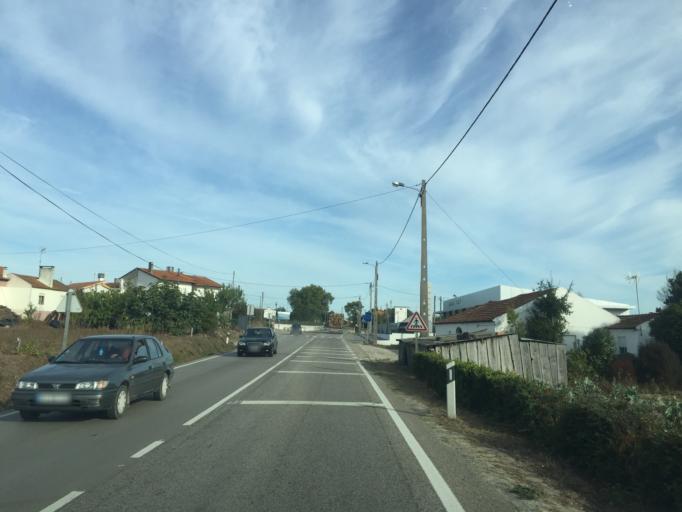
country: PT
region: Leiria
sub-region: Pombal
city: Lourical
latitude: 39.9979
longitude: -8.8040
